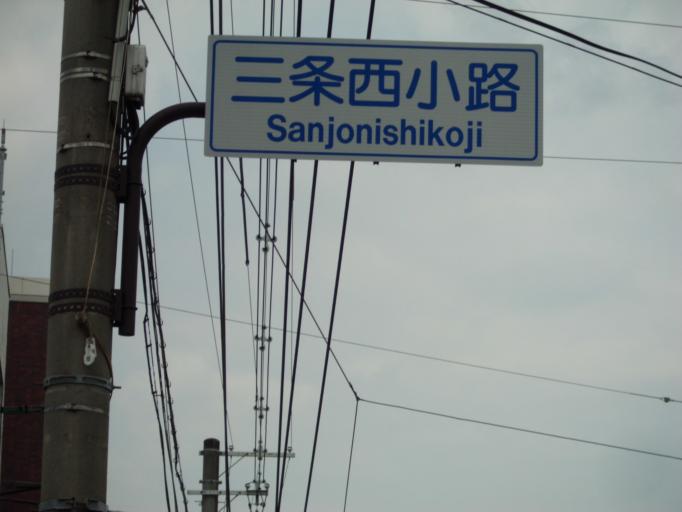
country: JP
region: Kyoto
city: Kyoto
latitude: 35.0083
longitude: 135.7318
